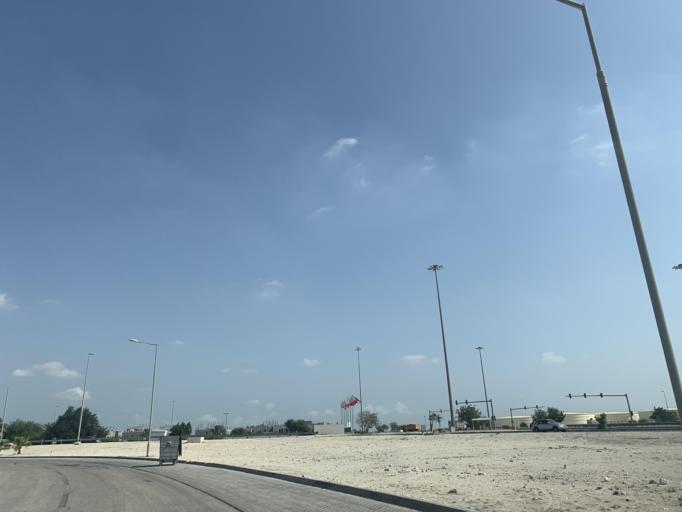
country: BH
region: Central Governorate
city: Madinat Hamad
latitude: 26.1213
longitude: 50.5057
